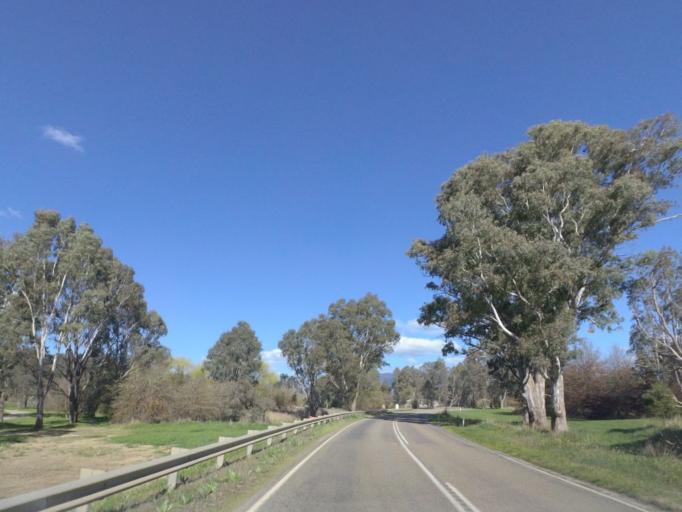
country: AU
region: Victoria
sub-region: Murrindindi
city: Alexandra
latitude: -37.2341
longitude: 145.7688
